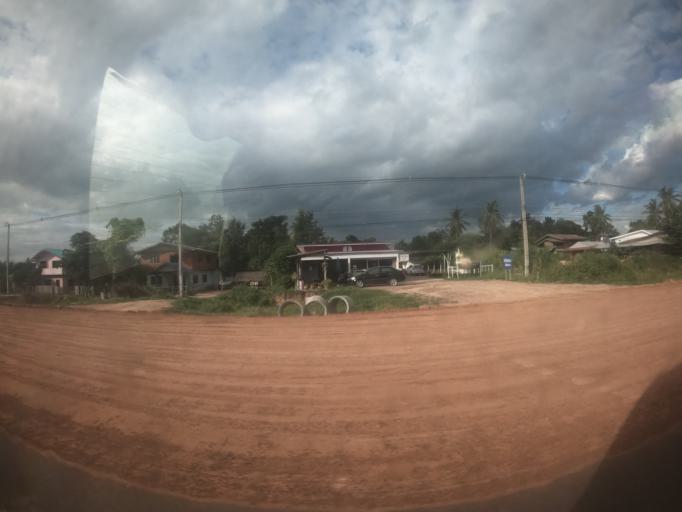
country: TH
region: Surin
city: Kap Choeng
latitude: 14.4982
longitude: 103.5660
